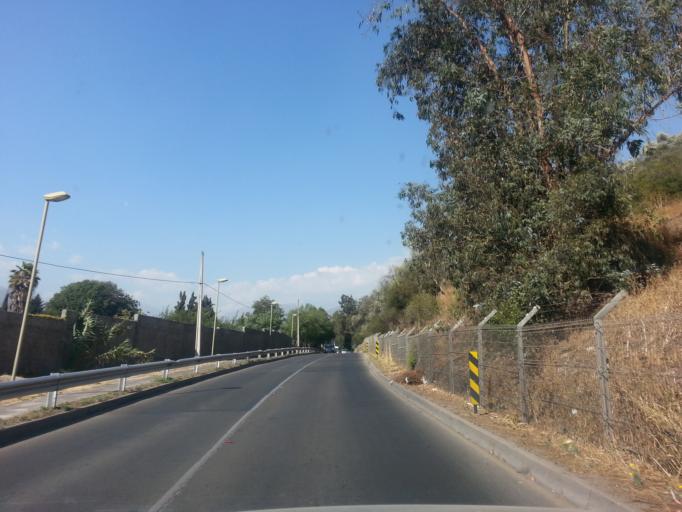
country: CL
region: Santiago Metropolitan
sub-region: Provincia de Santiago
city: Villa Presidente Frei, Nunoa, Santiago, Chile
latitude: -33.3827
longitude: -70.5147
